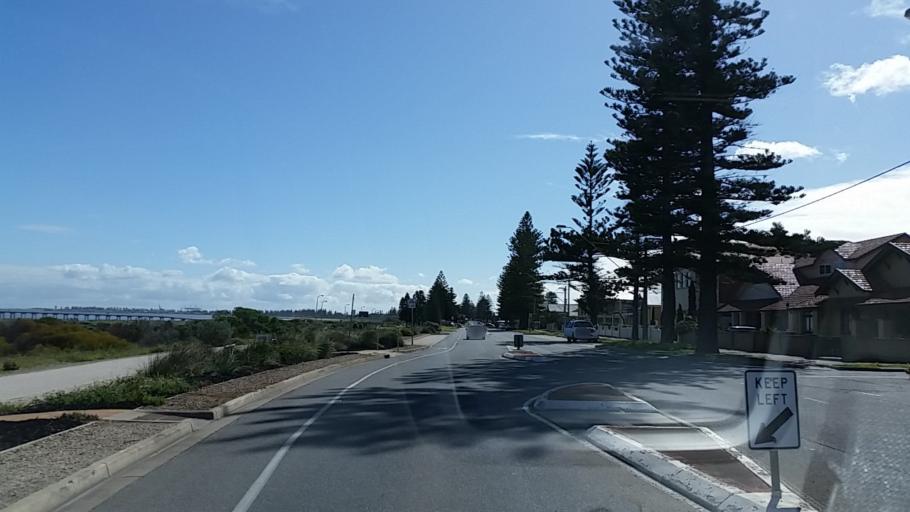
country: AU
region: South Australia
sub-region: Port Adelaide Enfield
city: Birkenhead
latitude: -34.8287
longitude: 138.4844
